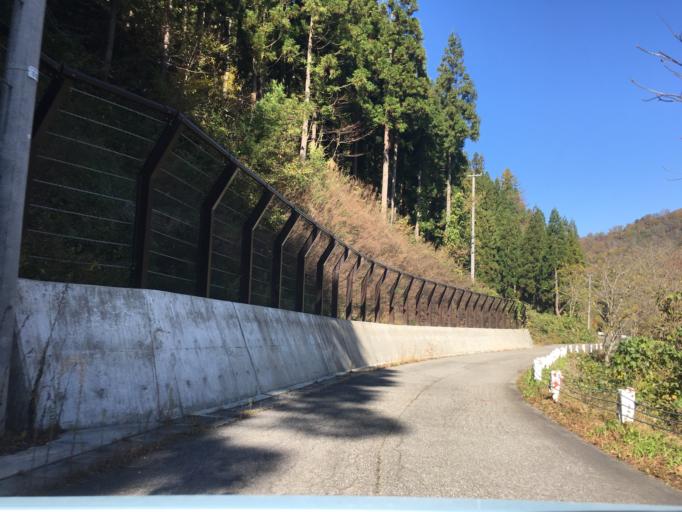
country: JP
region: Fukushima
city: Inawashiro
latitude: 37.4188
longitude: 139.9879
